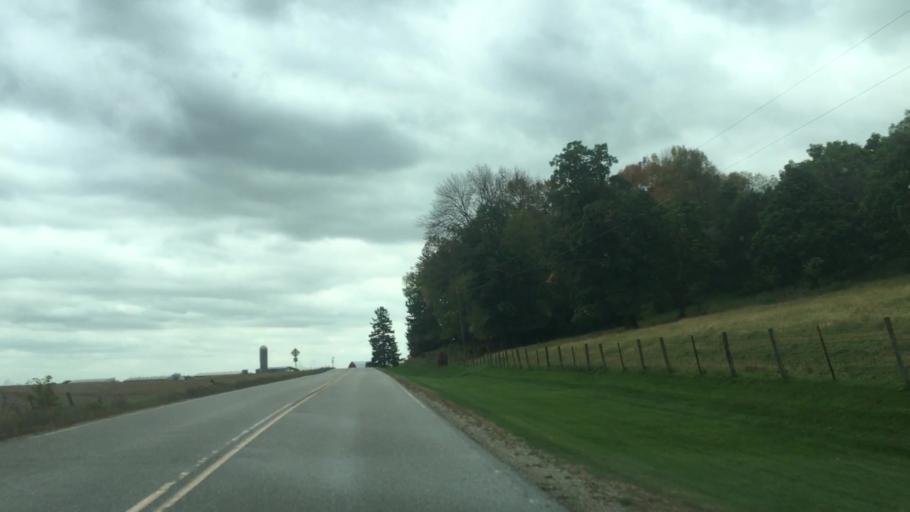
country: US
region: Minnesota
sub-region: Fillmore County
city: Preston
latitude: 43.7407
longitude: -92.0104
